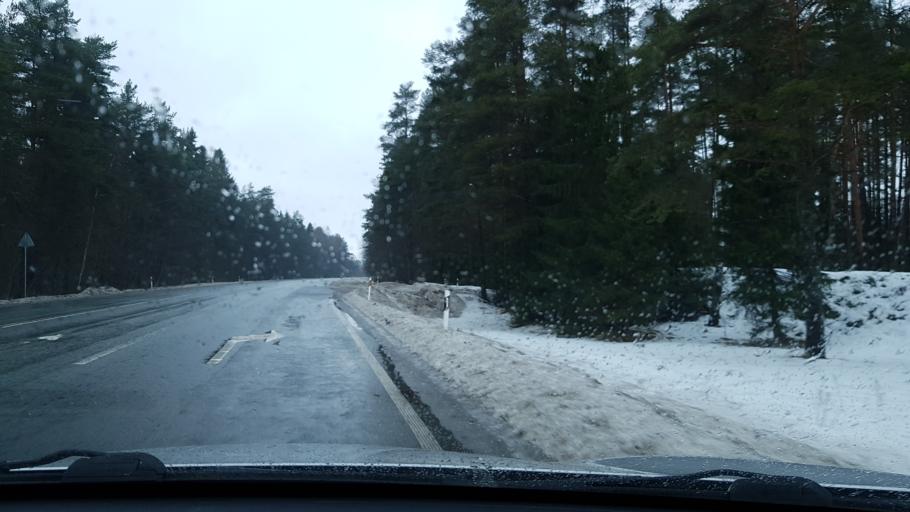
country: EE
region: Raplamaa
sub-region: Kohila vald
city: Kohila
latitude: 59.1631
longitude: 24.7722
